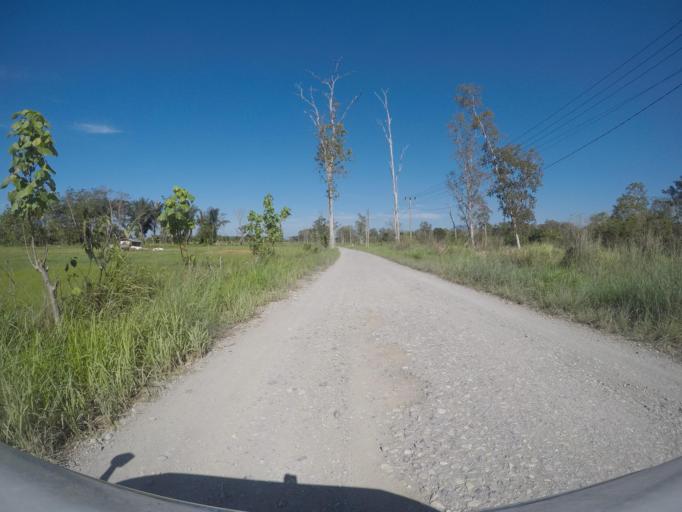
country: TL
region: Viqueque
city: Viqueque
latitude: -8.9354
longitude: 126.1230
